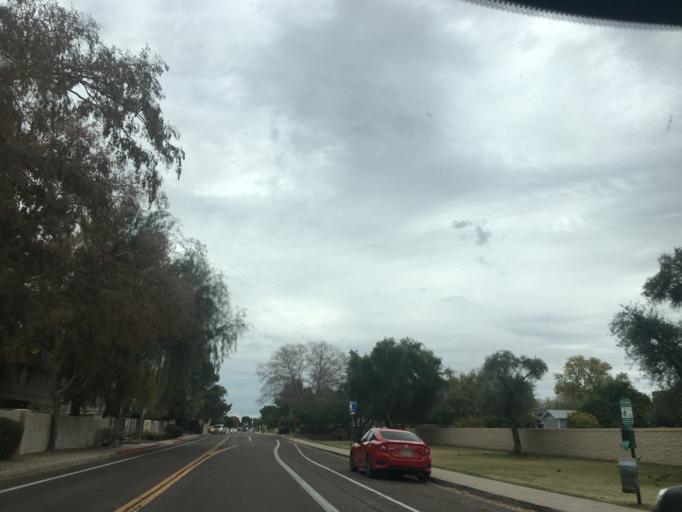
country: US
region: Arizona
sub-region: Maricopa County
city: Guadalupe
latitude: 33.3712
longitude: -111.9211
